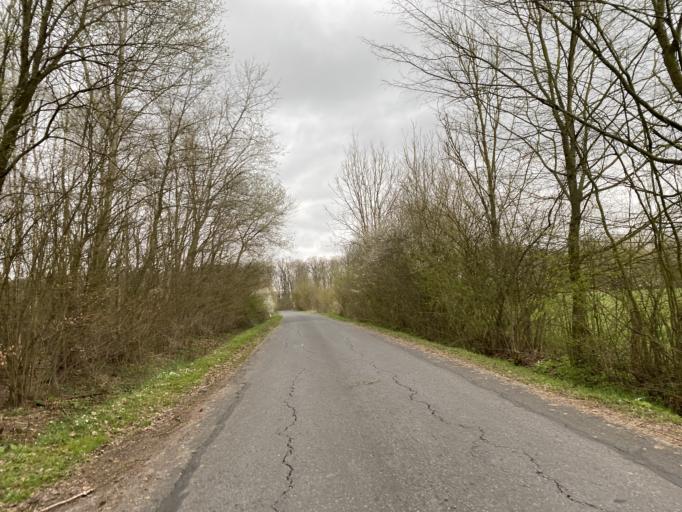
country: DE
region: North Rhine-Westphalia
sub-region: Regierungsbezirk Arnsberg
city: Welver
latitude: 51.6815
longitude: 7.9465
